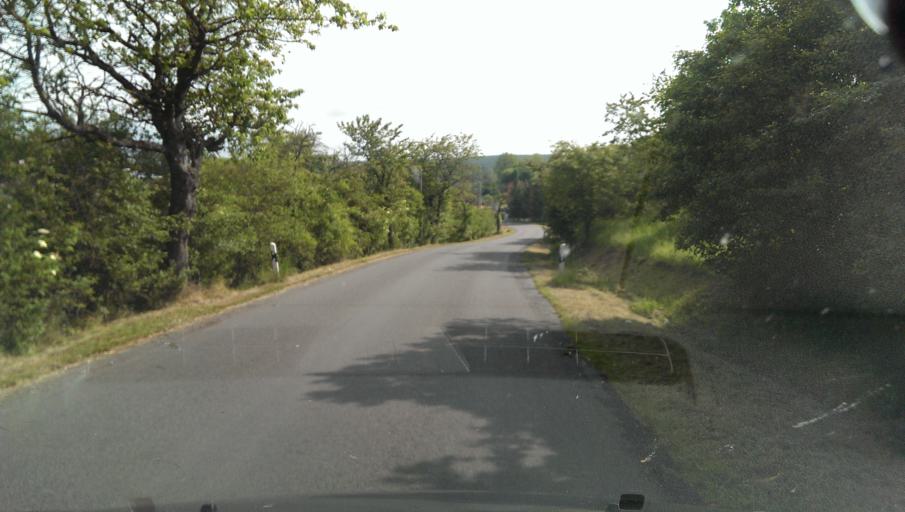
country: DE
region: Thuringia
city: Rittersdorf
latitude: 50.8442
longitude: 11.2486
